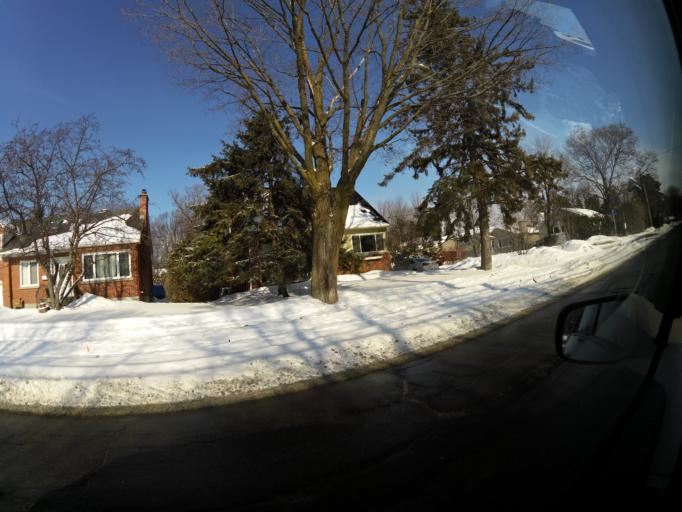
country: CA
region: Ontario
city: Ottawa
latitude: 45.3870
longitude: -75.6577
